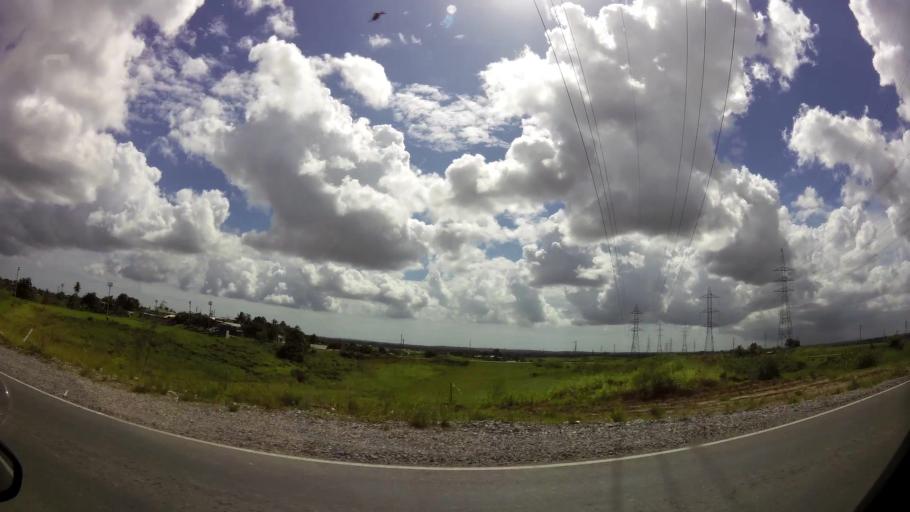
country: TT
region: Penal/Debe
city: Debe
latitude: 10.2183
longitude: -61.4605
